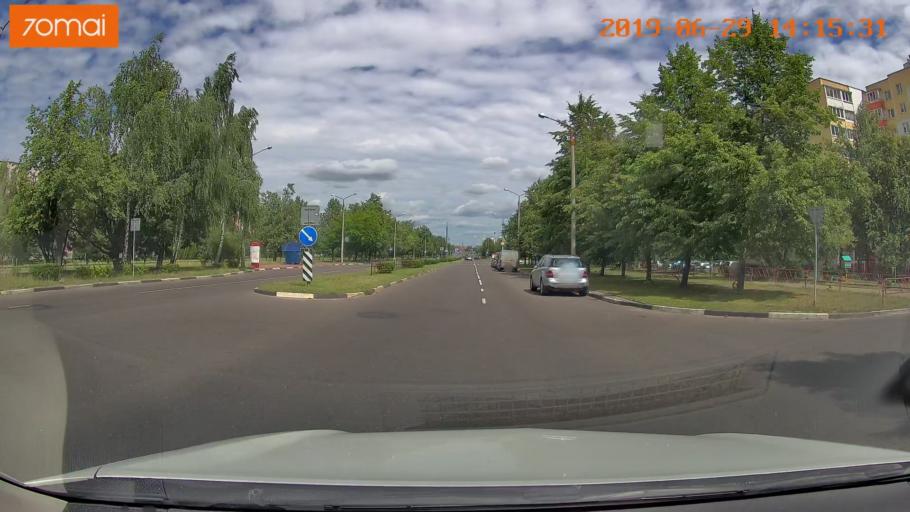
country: BY
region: Minsk
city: Salihorsk
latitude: 52.7924
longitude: 27.5224
